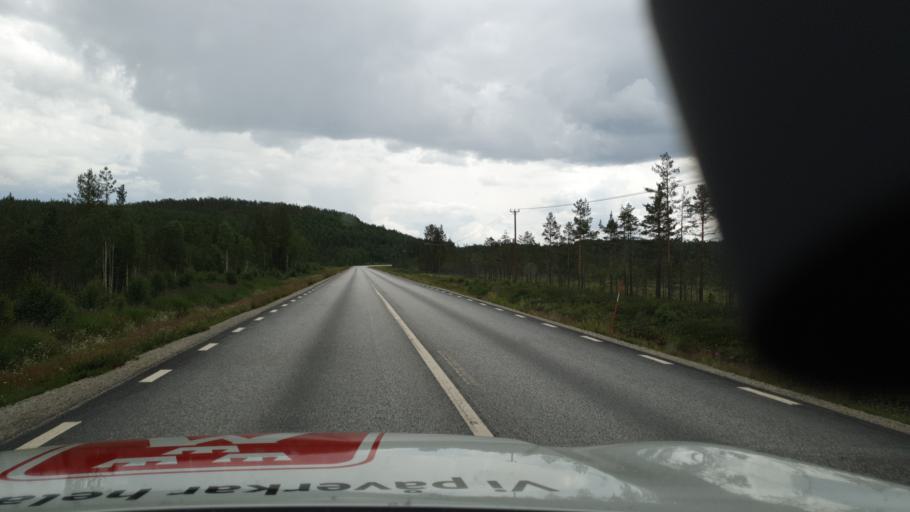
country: SE
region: Vaesterbotten
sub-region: Vannas Kommun
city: Vaennaes
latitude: 64.0439
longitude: 19.6870
